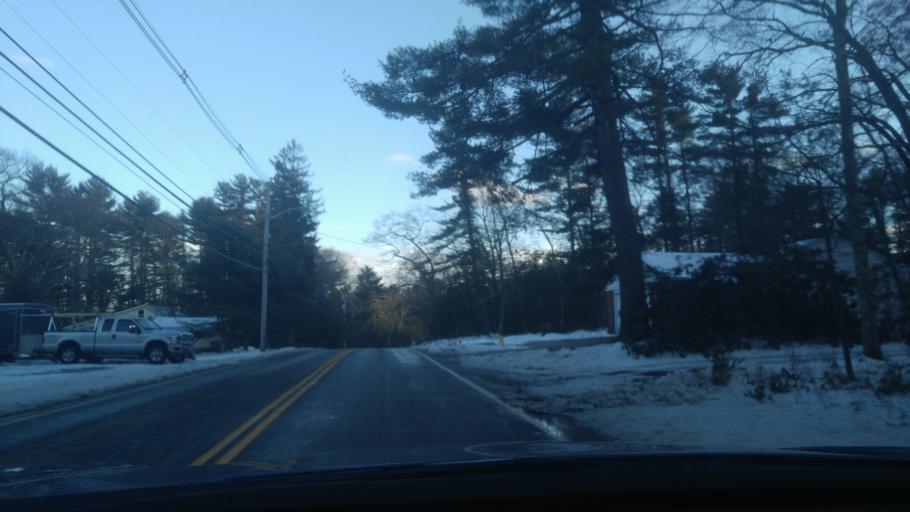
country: US
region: Rhode Island
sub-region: Kent County
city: West Greenwich
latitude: 41.6858
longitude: -71.6190
